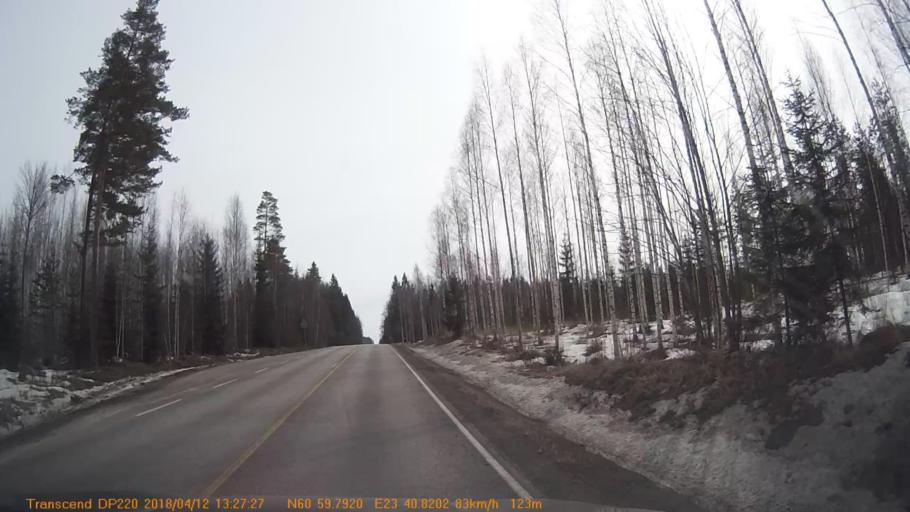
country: FI
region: Pirkanmaa
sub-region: Etelae-Pirkanmaa
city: Kylmaekoski
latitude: 60.9963
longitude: 23.6805
